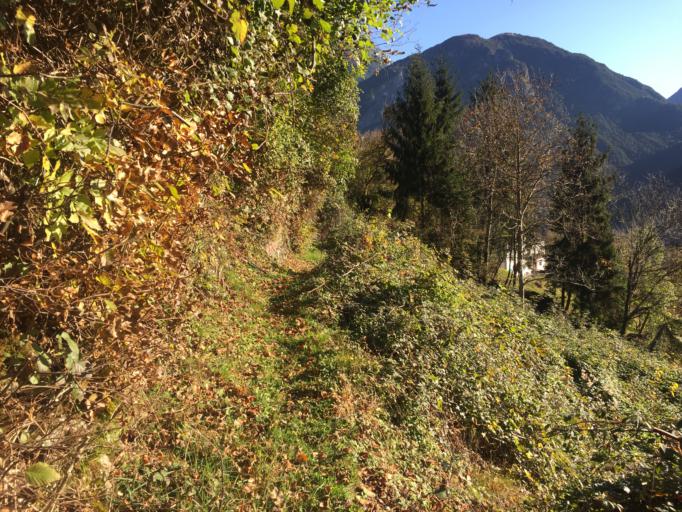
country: IT
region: Friuli Venezia Giulia
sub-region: Provincia di Udine
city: Chiusaforte
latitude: 46.4058
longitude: 13.2929
